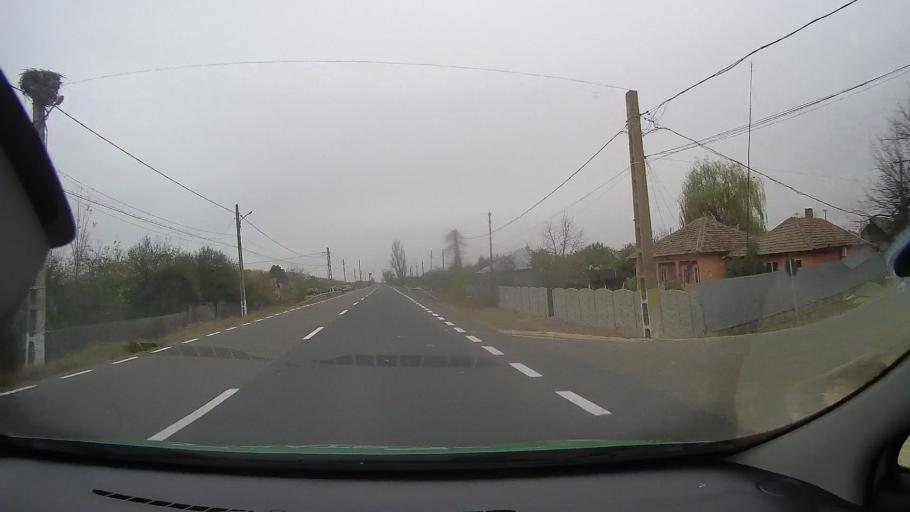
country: RO
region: Ialomita
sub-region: Comuna Giurgeni
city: Giurgeni
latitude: 44.7395
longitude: 27.8557
